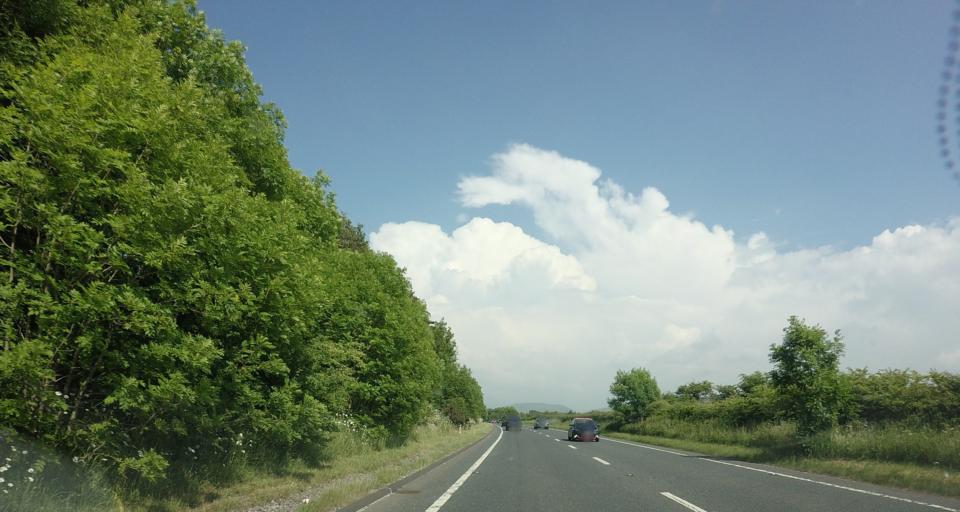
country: GB
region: England
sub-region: Cumbria
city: Cockermouth
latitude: 54.6502
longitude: -3.3520
